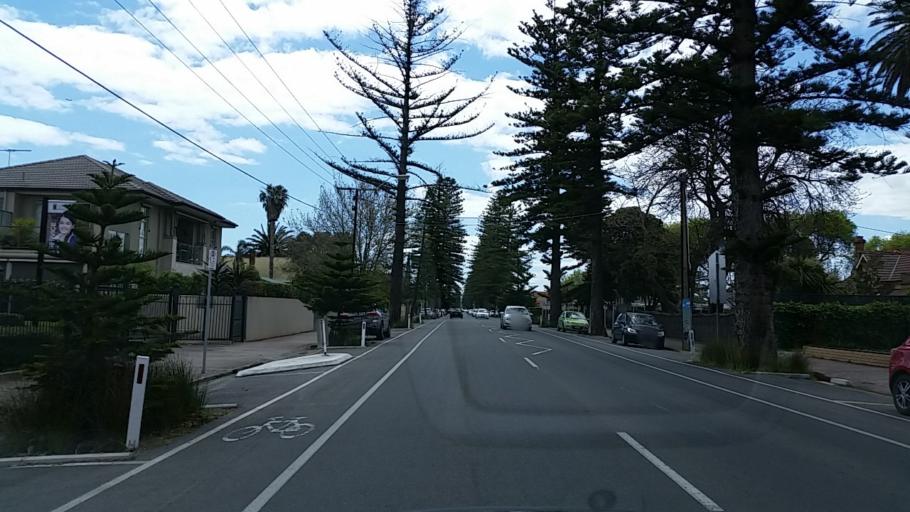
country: AU
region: South Australia
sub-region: Adelaide
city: Glenelg
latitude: -34.9838
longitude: 138.5180
